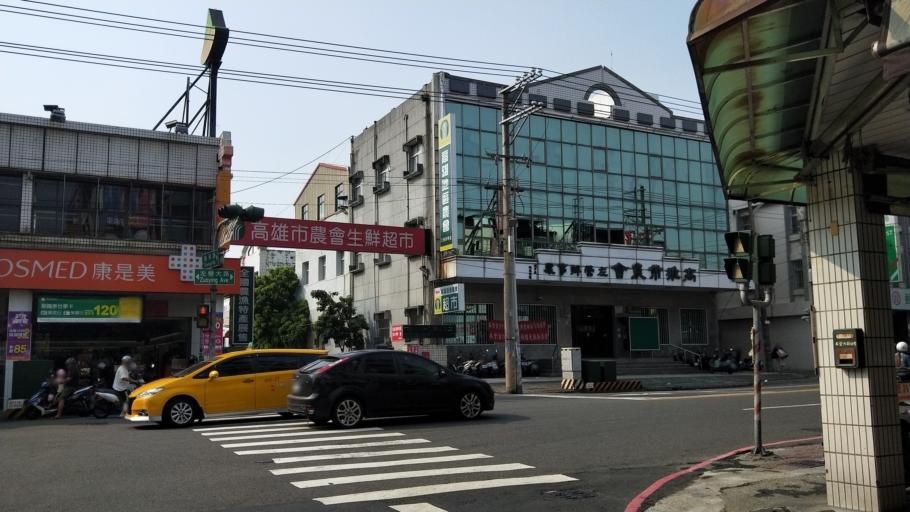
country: TW
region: Kaohsiung
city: Kaohsiung
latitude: 22.6817
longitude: 120.2883
